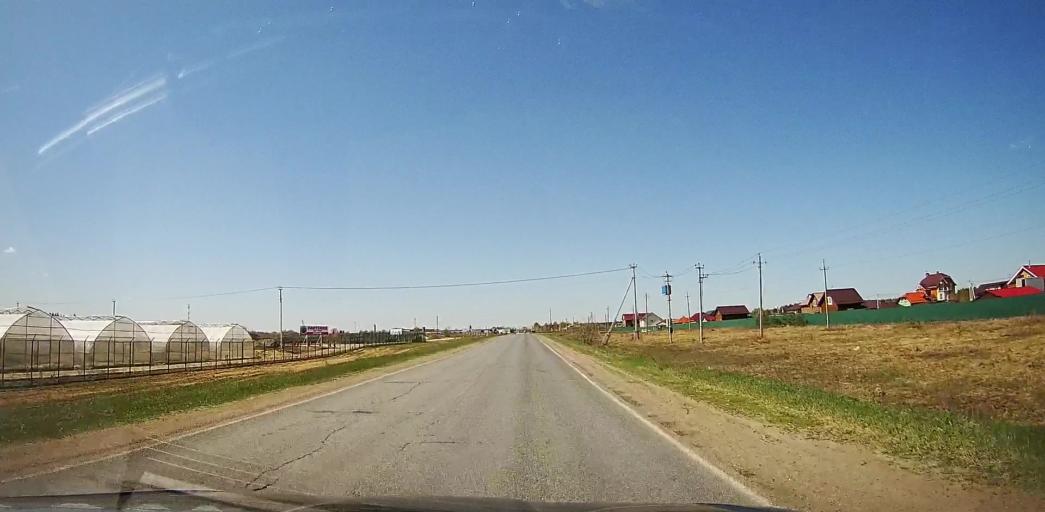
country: RU
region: Moskovskaya
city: Malyshevo
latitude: 55.4548
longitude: 38.3179
